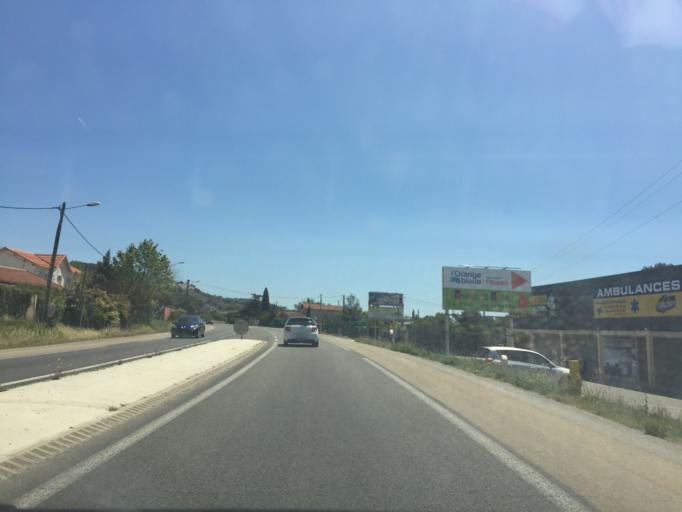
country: FR
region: Provence-Alpes-Cote d'Azur
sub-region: Departement des Bouches-du-Rhone
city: Rognac
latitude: 43.4750
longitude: 5.2280
